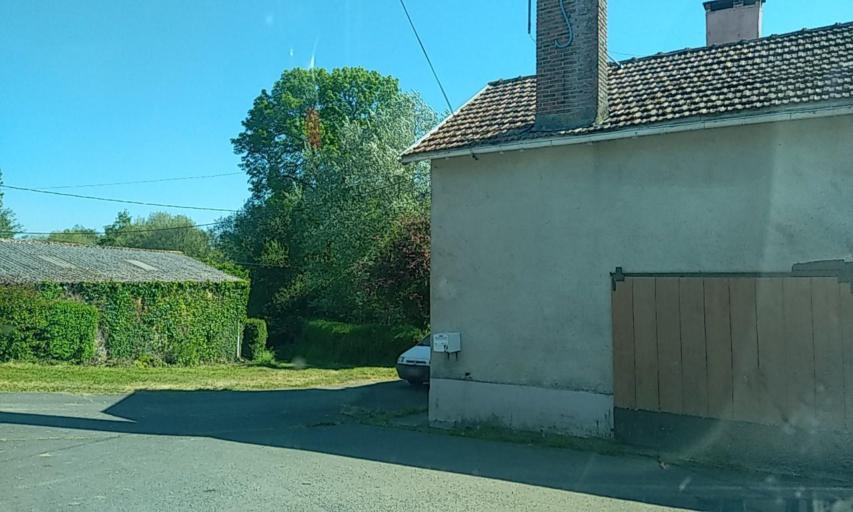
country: FR
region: Poitou-Charentes
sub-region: Departement des Deux-Sevres
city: Boisme
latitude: 46.7730
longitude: -0.4176
